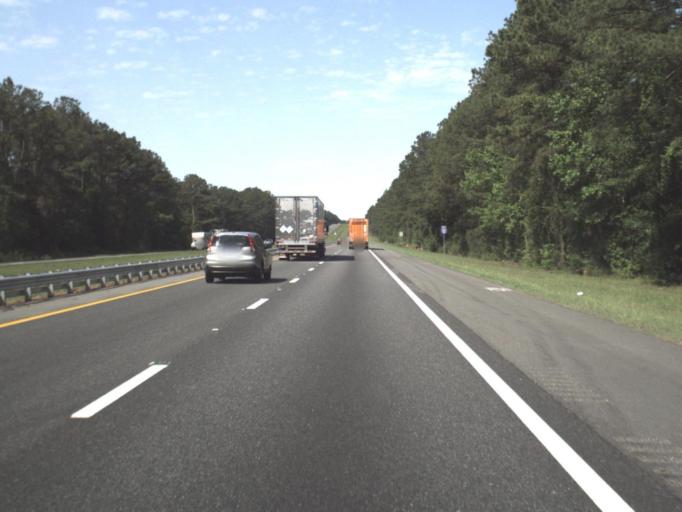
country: US
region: Florida
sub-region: Walton County
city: DeFuniak Springs
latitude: 30.7104
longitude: -85.9433
